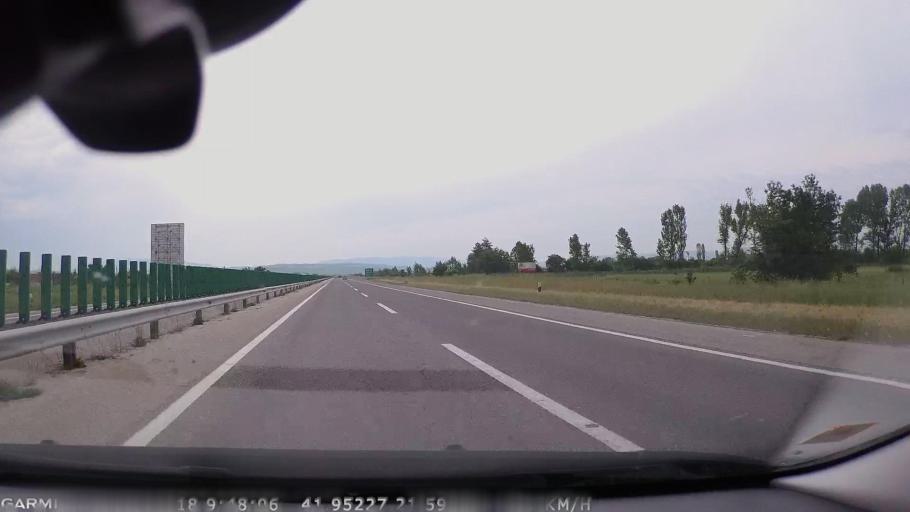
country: MK
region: Ilinden
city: Idrizovo
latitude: 41.9653
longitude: 21.5767
